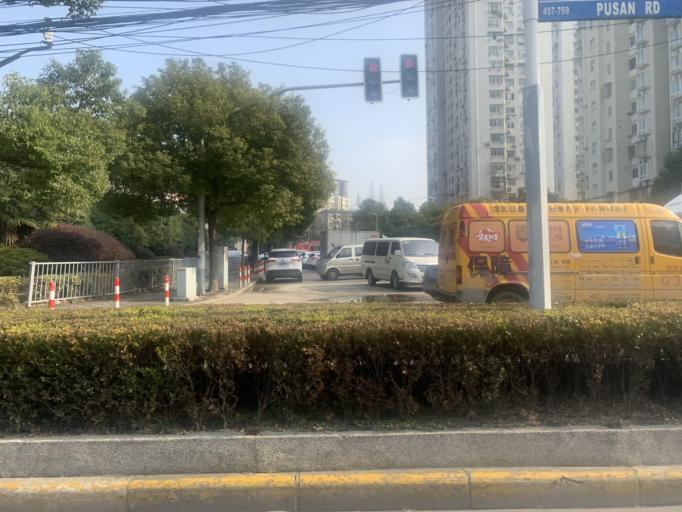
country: CN
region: Shanghai Shi
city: Huamu
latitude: 31.1861
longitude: 121.5144
